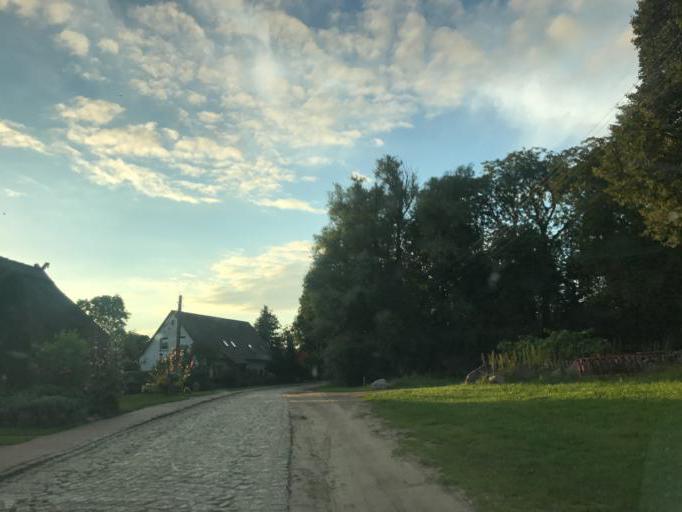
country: DE
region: Mecklenburg-Vorpommern
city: Rechlin
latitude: 53.3396
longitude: 12.8432
